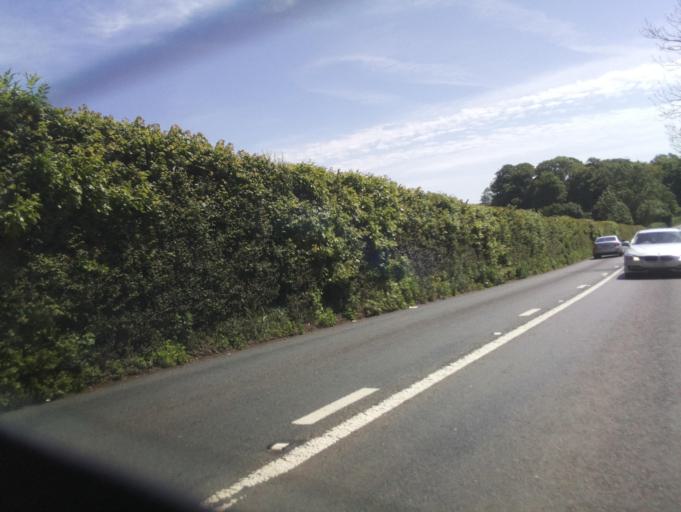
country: GB
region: England
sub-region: Devon
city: Topsham
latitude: 50.6783
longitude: -3.4437
